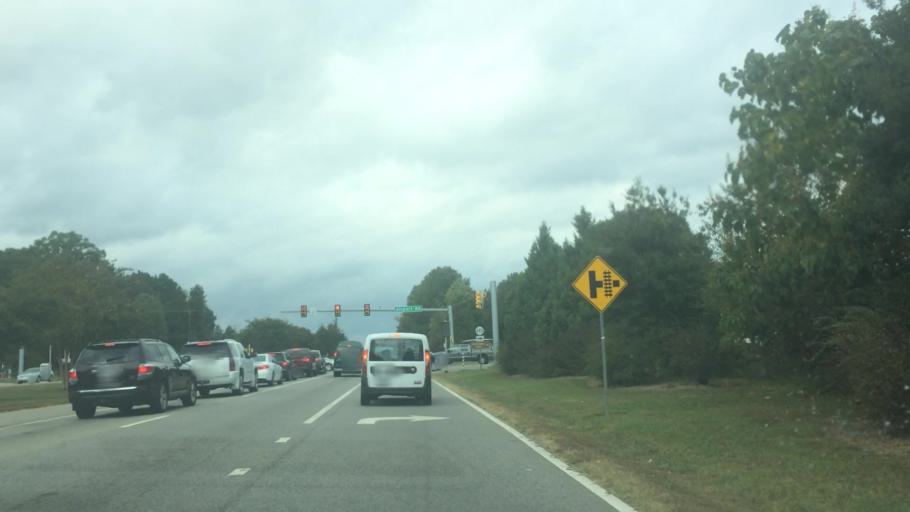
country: US
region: Virginia
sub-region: James City County
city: Williamsburg
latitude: 37.3121
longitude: -76.7317
